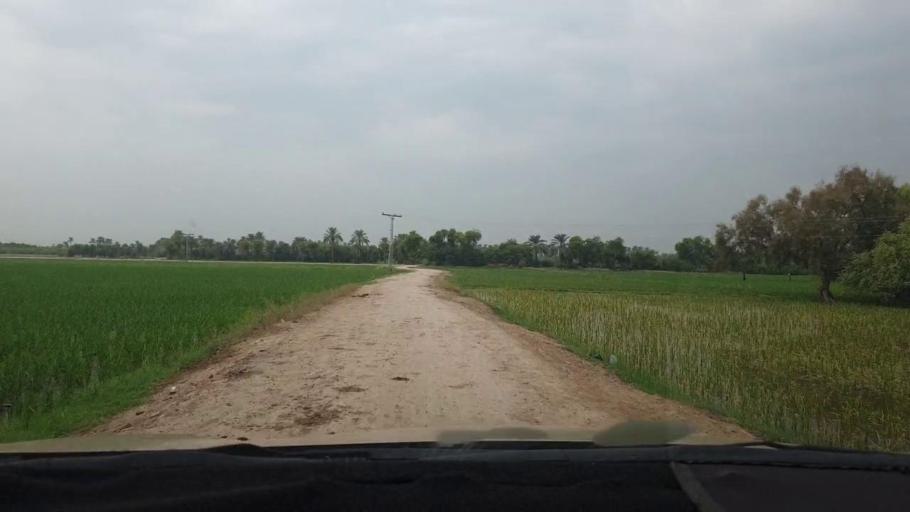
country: PK
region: Sindh
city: Larkana
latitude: 27.5768
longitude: 68.2440
